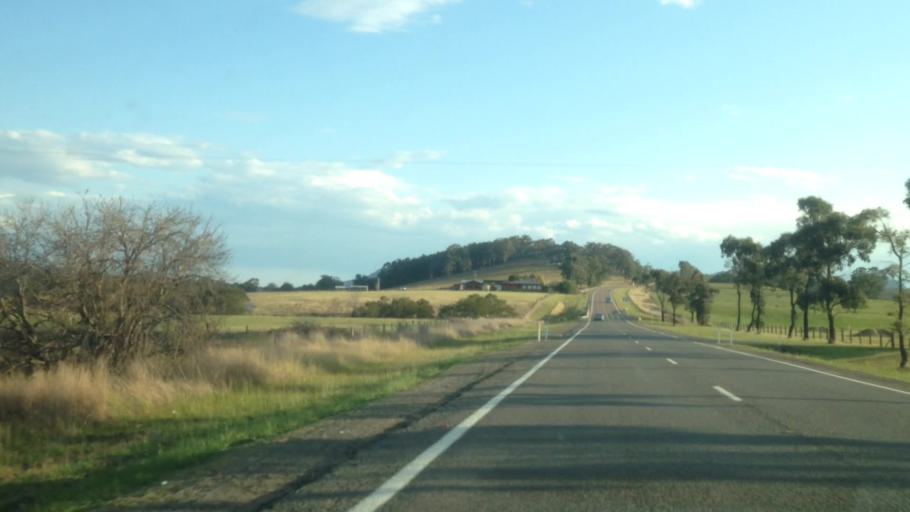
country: AU
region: New South Wales
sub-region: Cessnock
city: Kurri Kurri
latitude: -32.8766
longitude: 151.4748
